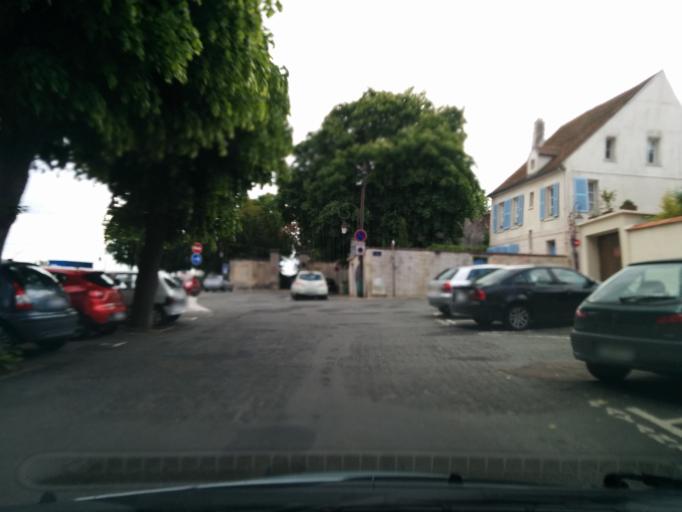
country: FR
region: Ile-de-France
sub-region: Departement des Yvelines
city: Mantes-la-Jolie
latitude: 48.9900
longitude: 1.7201
